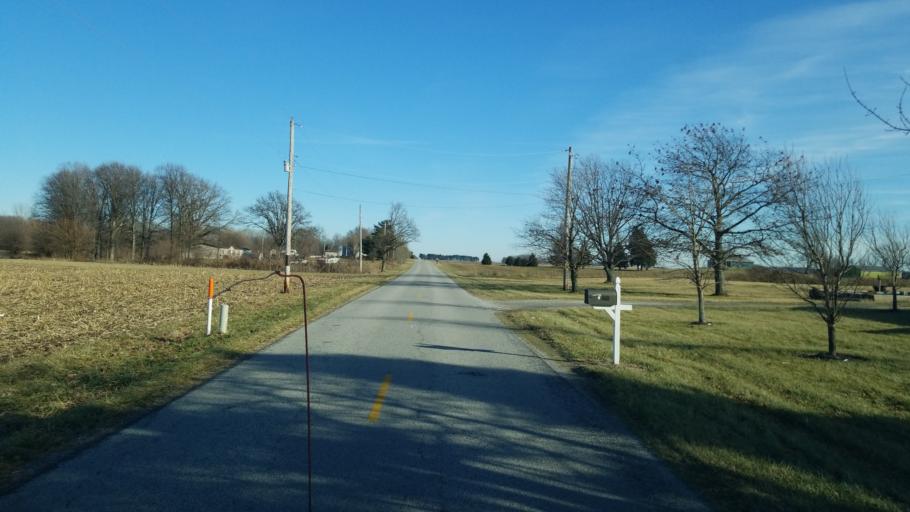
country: US
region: Ohio
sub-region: Sandusky County
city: Green Springs
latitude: 41.2559
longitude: -83.0089
